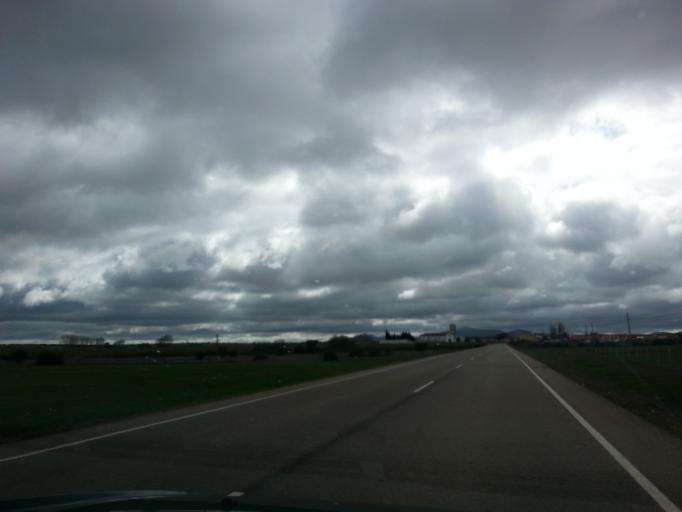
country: ES
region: Castille and Leon
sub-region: Provincia de Salamanca
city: Abusejo
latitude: 40.7158
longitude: -6.1461
